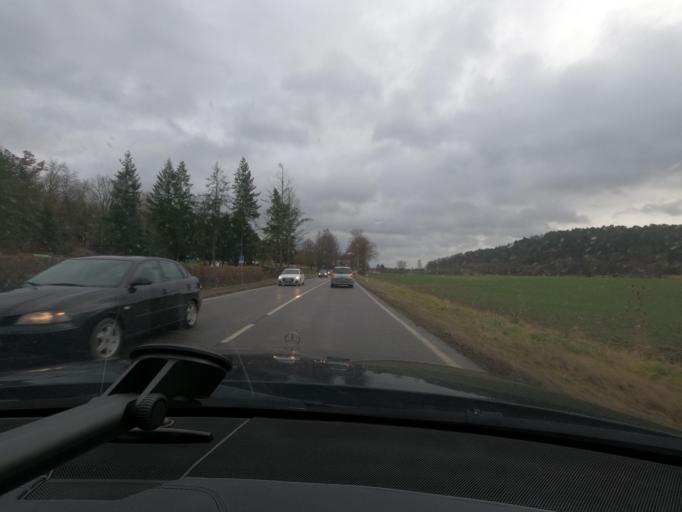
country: DE
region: Hesse
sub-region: Regierungsbezirk Kassel
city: Volkmarsen
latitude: 51.4063
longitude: 9.1369
